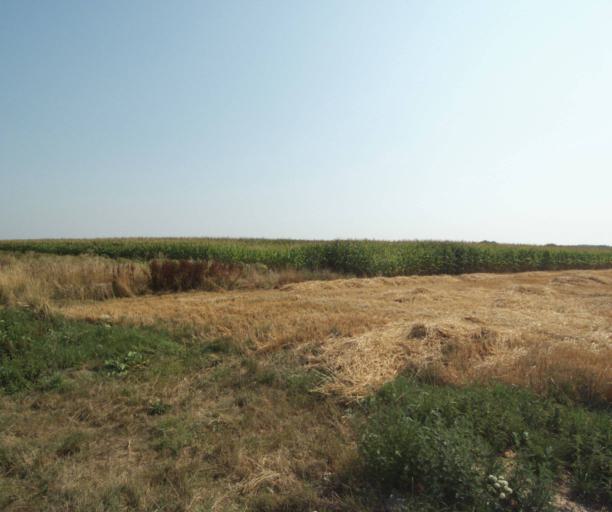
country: FR
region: Nord-Pas-de-Calais
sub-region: Departement du Nord
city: Quesnoy-sur-Deule
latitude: 50.7076
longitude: 2.9740
